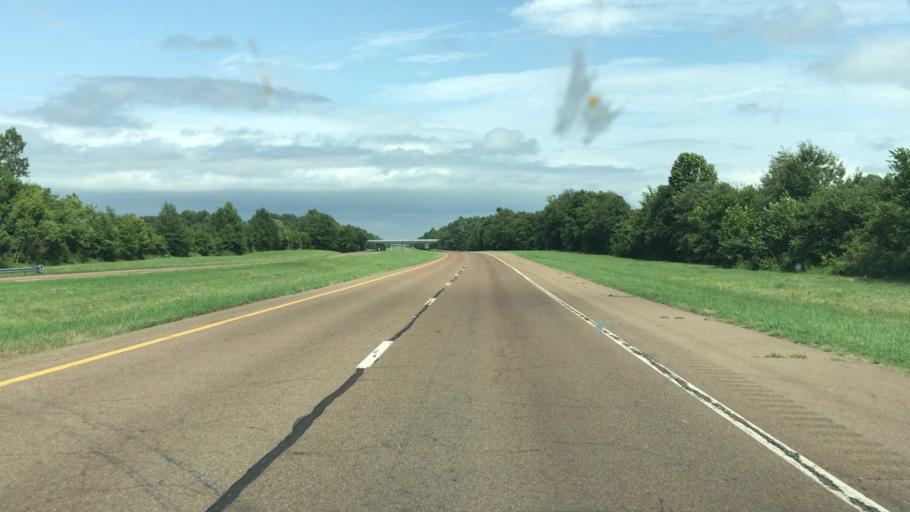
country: US
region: Tennessee
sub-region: Obion County
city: South Fulton
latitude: 36.4794
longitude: -88.9475
